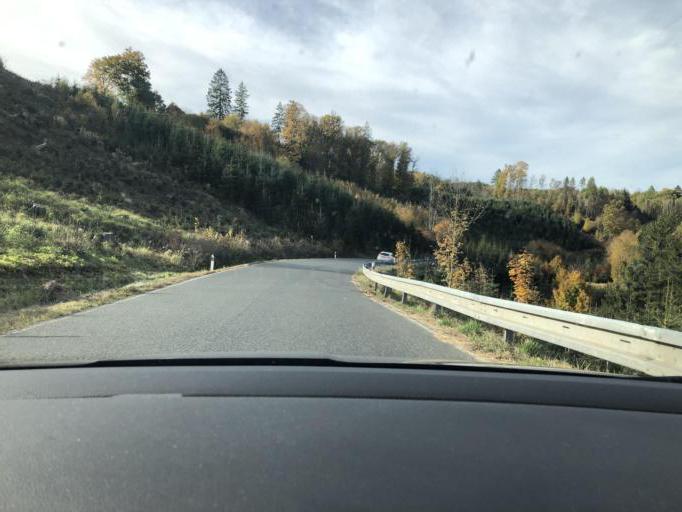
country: CZ
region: Central Bohemia
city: Divisov
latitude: 49.8033
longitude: 14.9272
